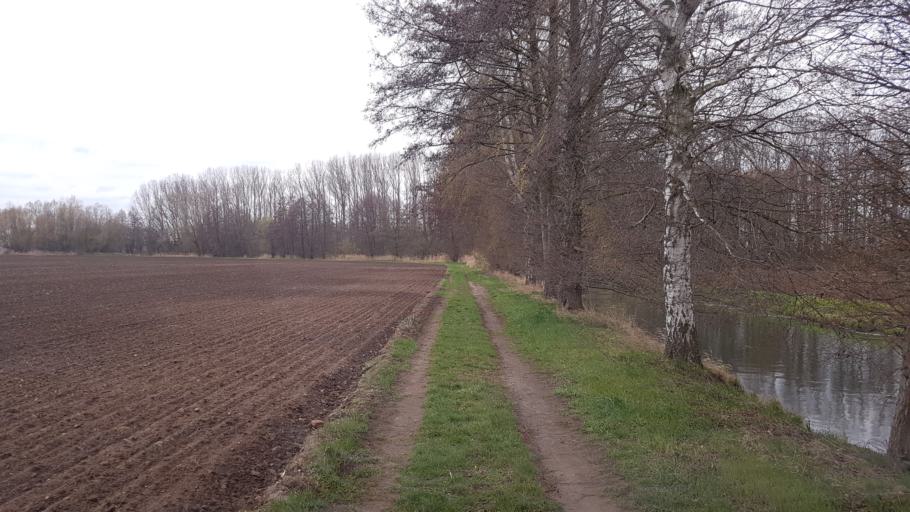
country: DE
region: Brandenburg
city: Doberlug-Kirchhain
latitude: 51.6499
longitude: 13.5594
